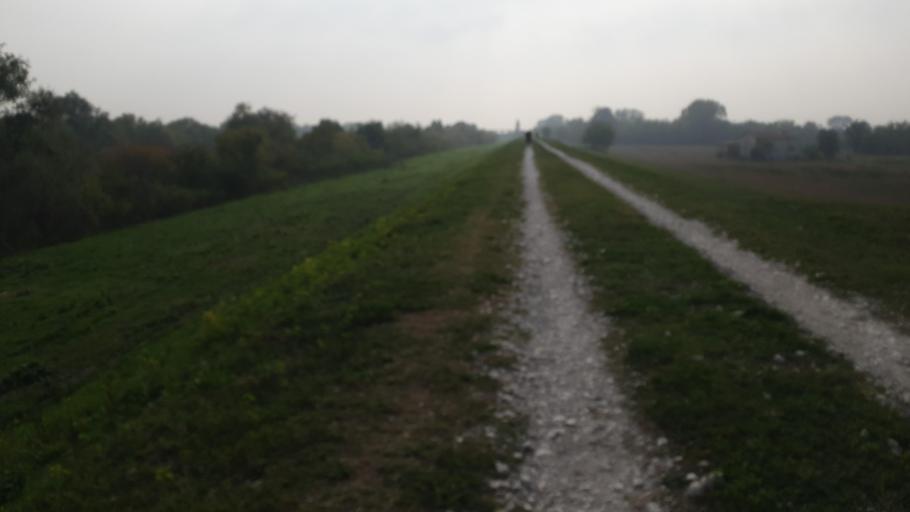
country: IT
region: Veneto
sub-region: Provincia di Venezia
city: Campolongo Maggiore
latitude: 45.3322
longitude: 12.0611
